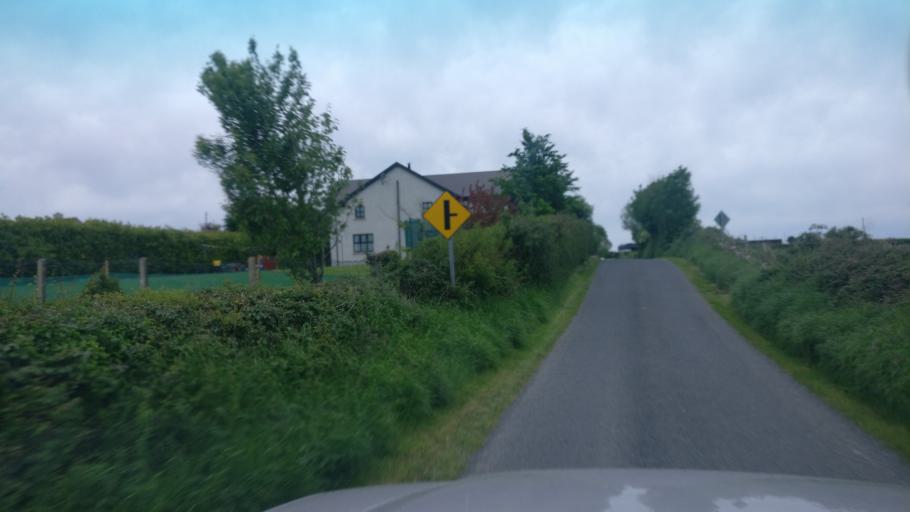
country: IE
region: Connaught
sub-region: County Galway
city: Portumna
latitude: 53.1282
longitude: -8.2895
